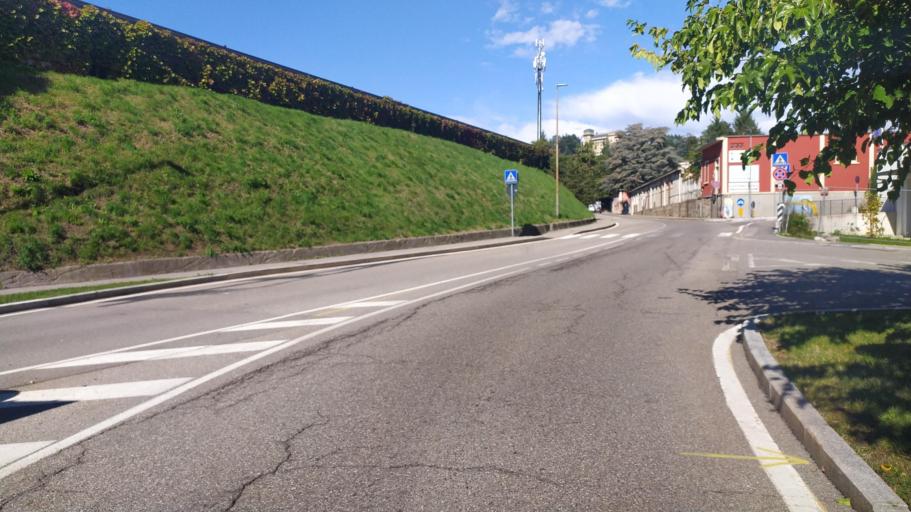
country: IT
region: Lombardy
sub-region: Provincia di Varese
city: Varese
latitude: 45.8140
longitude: 8.8090
